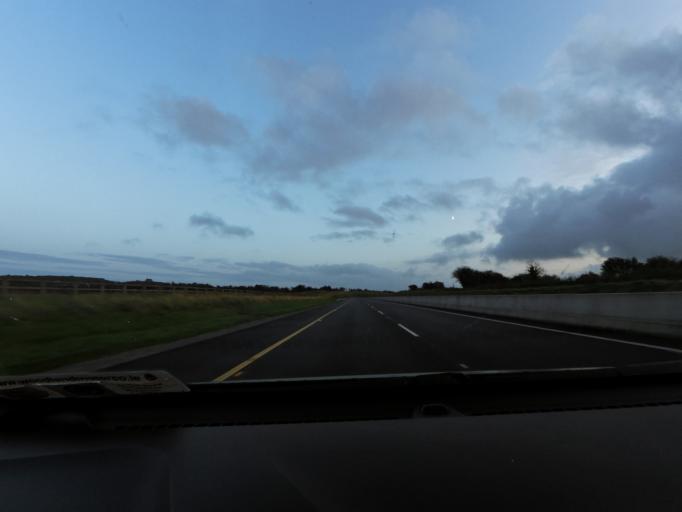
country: IE
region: Connaught
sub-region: County Galway
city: Athenry
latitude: 53.3700
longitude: -8.7901
